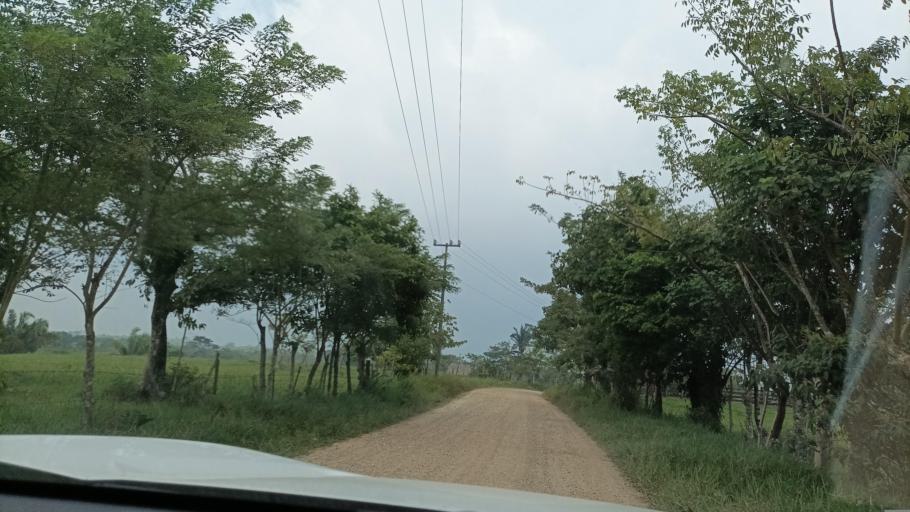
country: MX
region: Tabasco
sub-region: Huimanguillo
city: Francisco Rueda
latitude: 17.5947
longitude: -94.1979
